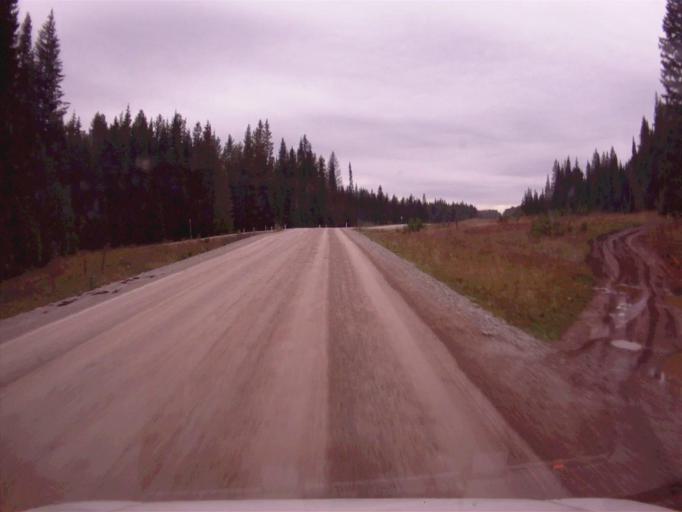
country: RU
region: Chelyabinsk
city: Nyazepetrovsk
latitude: 56.0565
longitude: 59.5532
